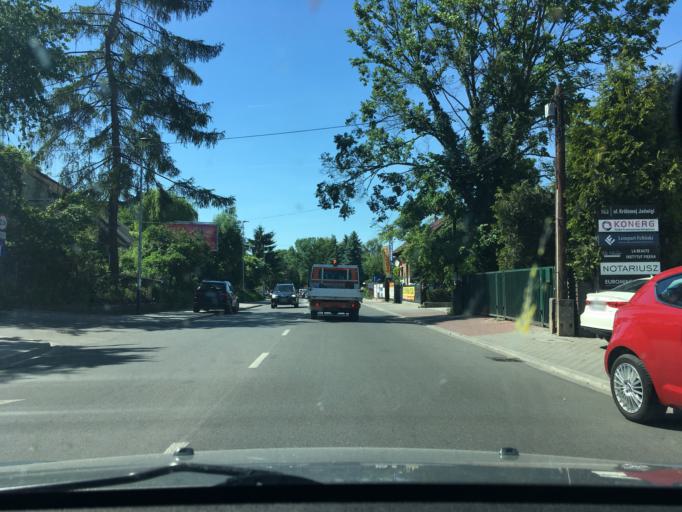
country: PL
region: Lesser Poland Voivodeship
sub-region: Krakow
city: Krakow
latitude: 50.0576
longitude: 19.9002
